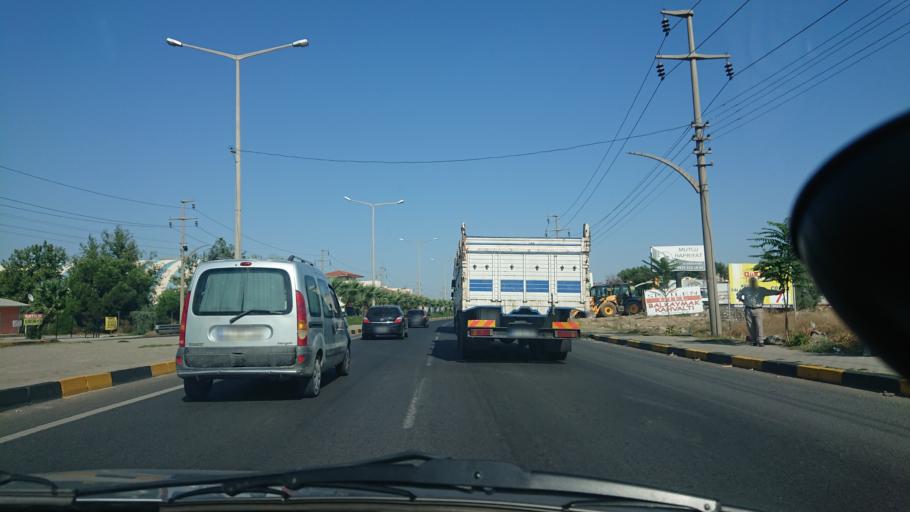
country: TR
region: Manisa
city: Turgutlu
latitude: 38.4948
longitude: 27.7217
